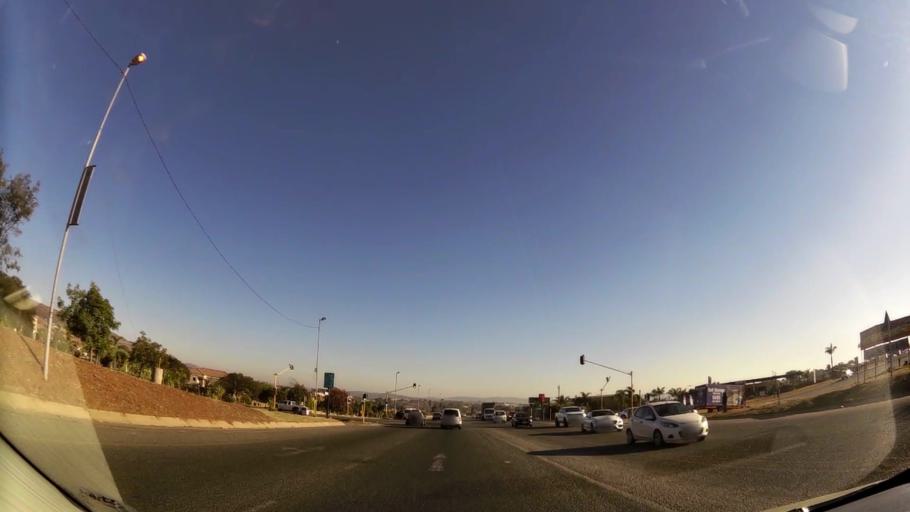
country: ZA
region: Gauteng
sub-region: West Rand District Municipality
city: Muldersdriseloop
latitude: -26.0694
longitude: 27.8505
